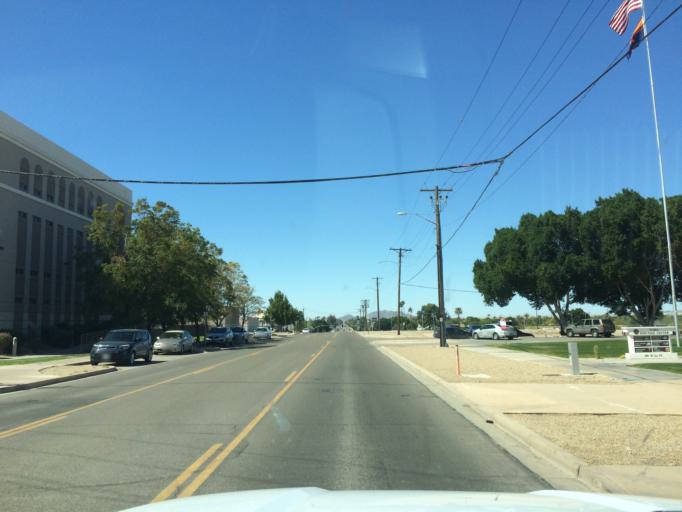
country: US
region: Arizona
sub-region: Yuma County
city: Yuma
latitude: 32.7252
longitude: -114.6213
